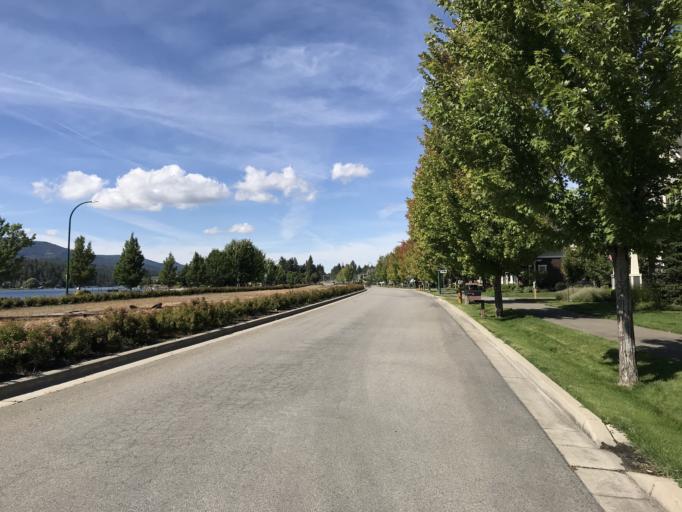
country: US
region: Idaho
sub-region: Kootenai County
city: Coeur d'Alene
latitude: 47.7009
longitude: -116.8412
